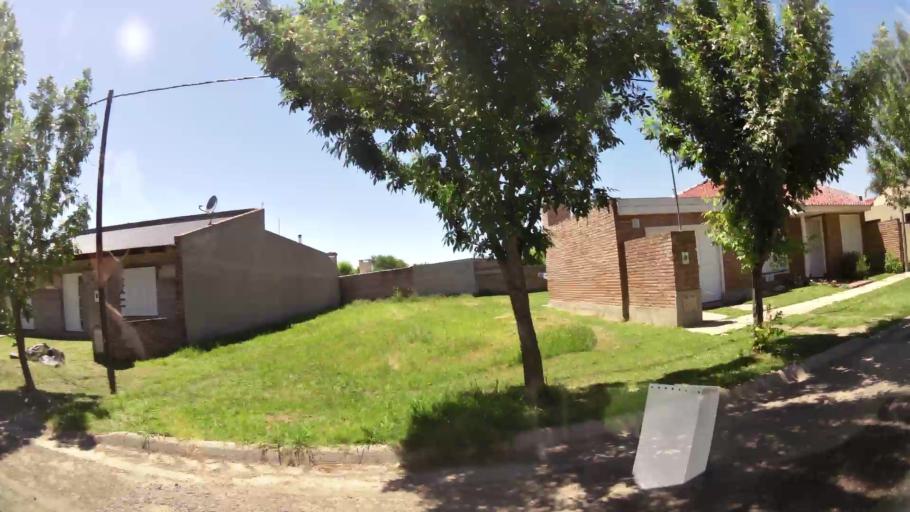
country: AR
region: Santa Fe
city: Esperanza
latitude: -31.3944
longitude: -61.0861
